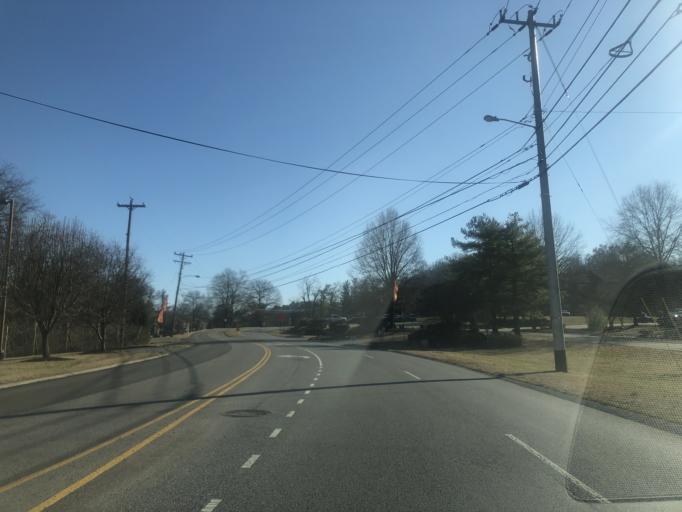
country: US
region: Tennessee
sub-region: Rutherford County
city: La Vergne
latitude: 36.0422
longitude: -86.6615
